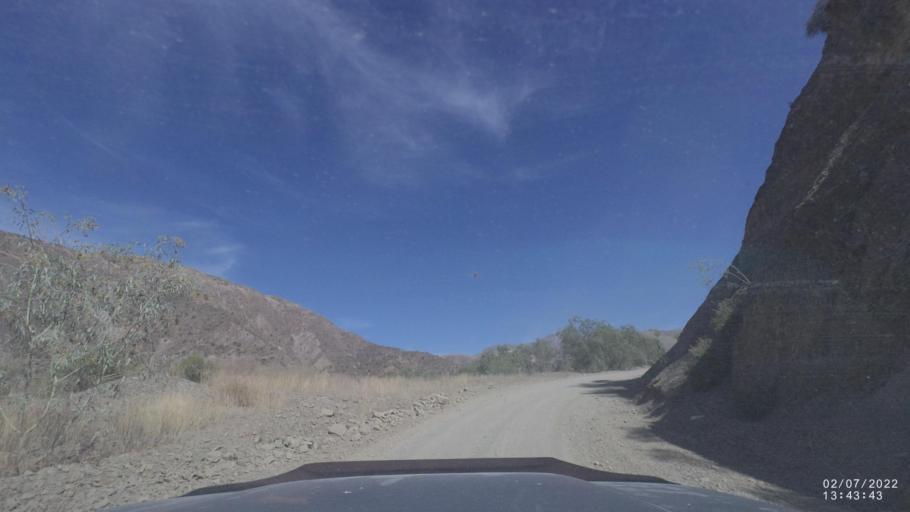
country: BO
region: Cochabamba
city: Irpa Irpa
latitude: -17.8049
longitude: -66.3611
